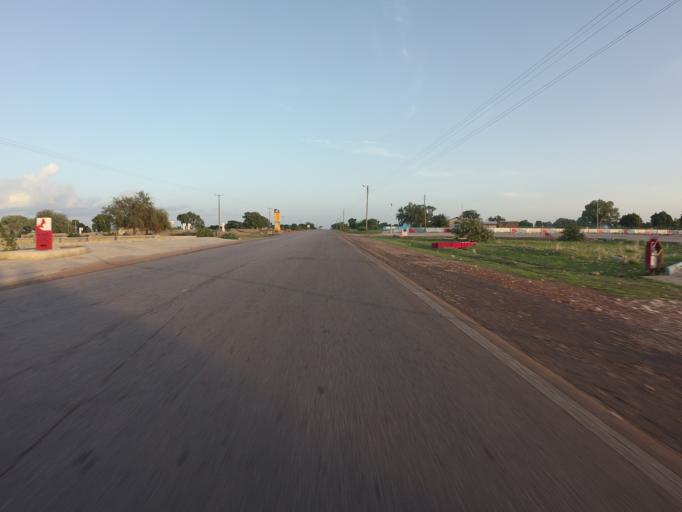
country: GH
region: Upper East
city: Navrongo
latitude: 10.9515
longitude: -1.0957
